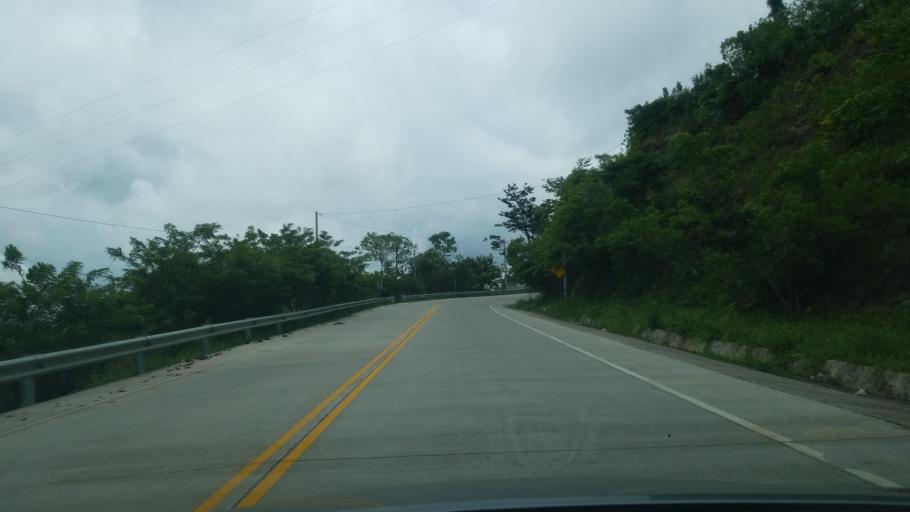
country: HN
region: Copan
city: San Jeronimo
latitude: 14.9548
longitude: -88.9078
